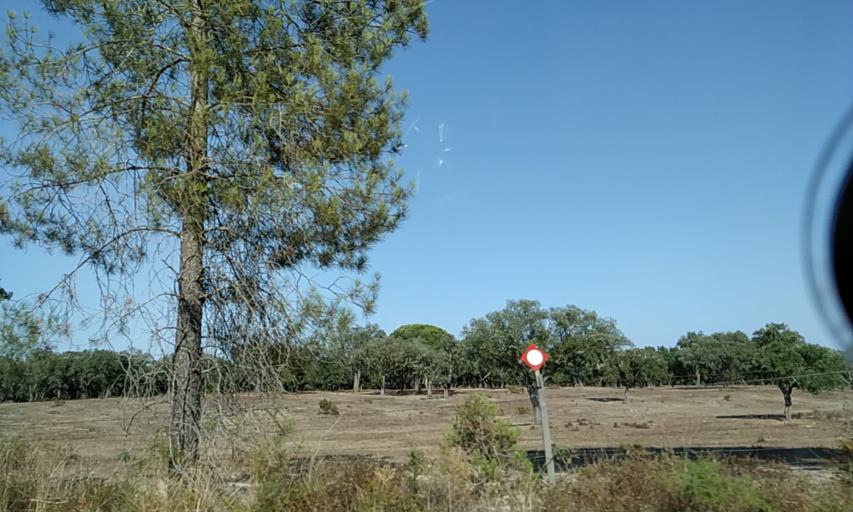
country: PT
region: Santarem
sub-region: Coruche
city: Coruche
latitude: 38.9157
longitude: -8.5250
